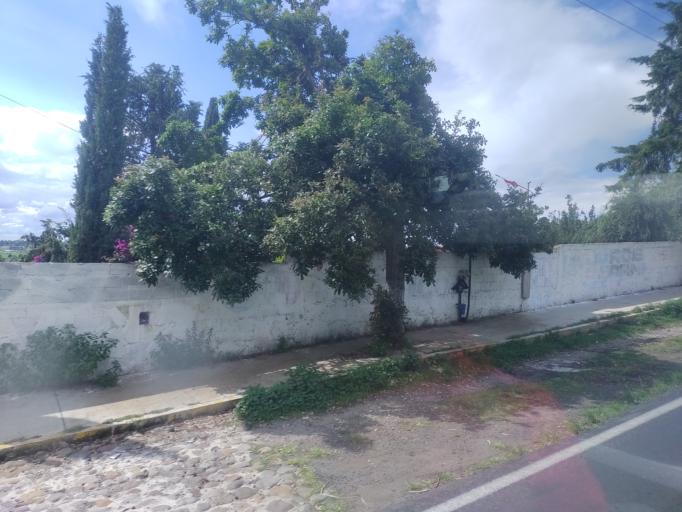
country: MX
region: Mexico
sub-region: Aculco
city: La Soledad Barrio
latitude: 20.0926
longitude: -99.7933
